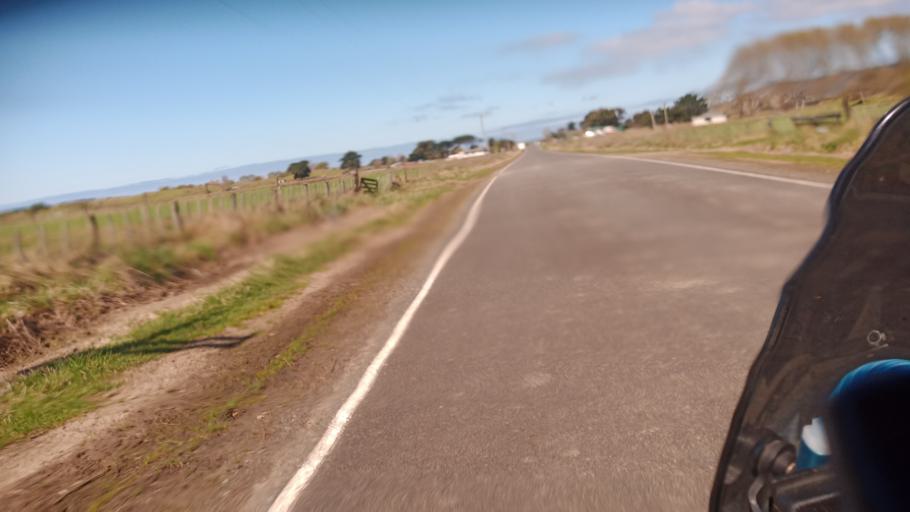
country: NZ
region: Gisborne
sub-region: Gisborne District
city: Gisborne
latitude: -39.0459
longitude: 177.8630
